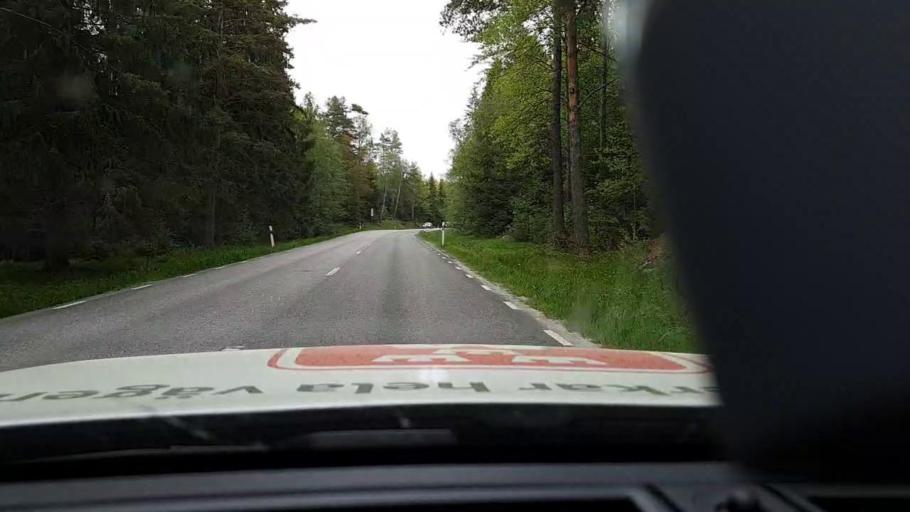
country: SE
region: Stockholm
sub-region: Haninge Kommun
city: Haninge
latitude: 59.1489
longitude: 18.1800
